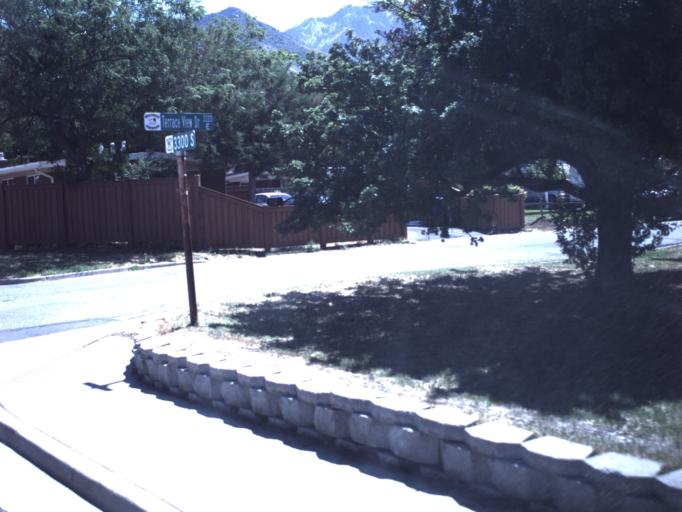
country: US
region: Utah
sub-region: Salt Lake County
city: East Millcreek
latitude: 40.6998
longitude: -111.8027
